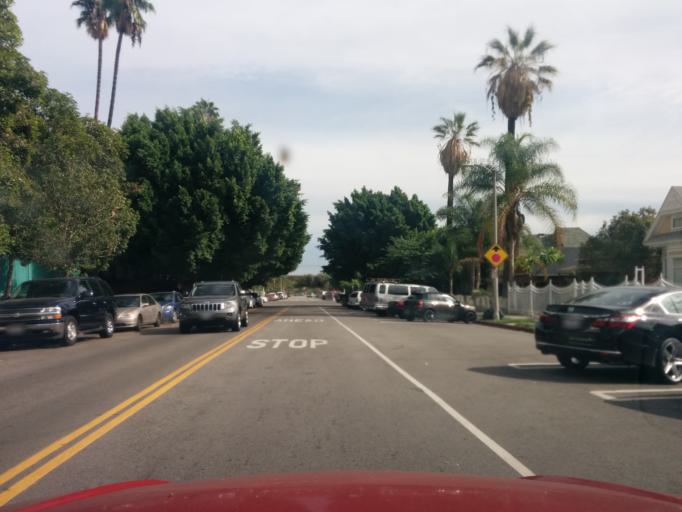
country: US
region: California
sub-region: Los Angeles County
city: Boyle Heights
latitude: 34.0479
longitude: -118.2178
